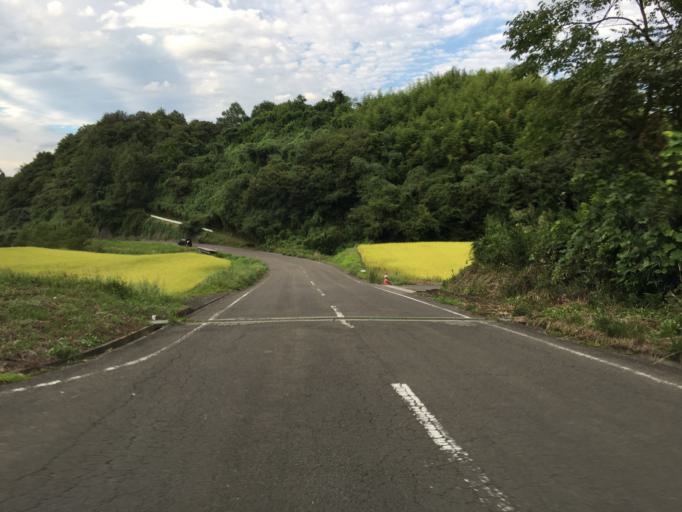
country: JP
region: Fukushima
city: Nihommatsu
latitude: 37.5876
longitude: 140.4984
